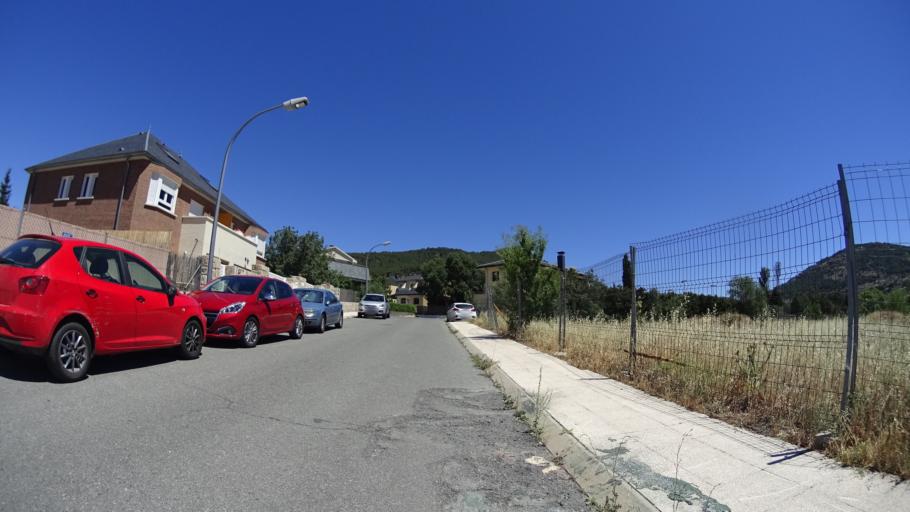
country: ES
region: Madrid
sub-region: Provincia de Madrid
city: Collado Mediano
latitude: 40.6891
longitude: -4.0268
